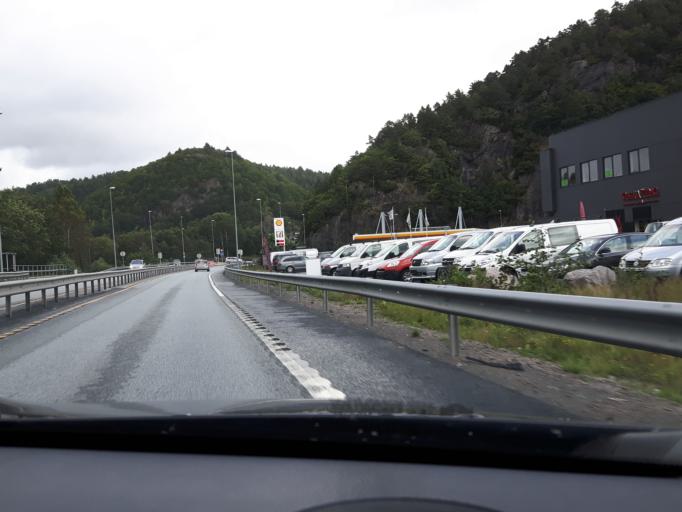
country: NO
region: Vest-Agder
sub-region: Songdalen
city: Nodeland
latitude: 58.1344
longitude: 7.8555
